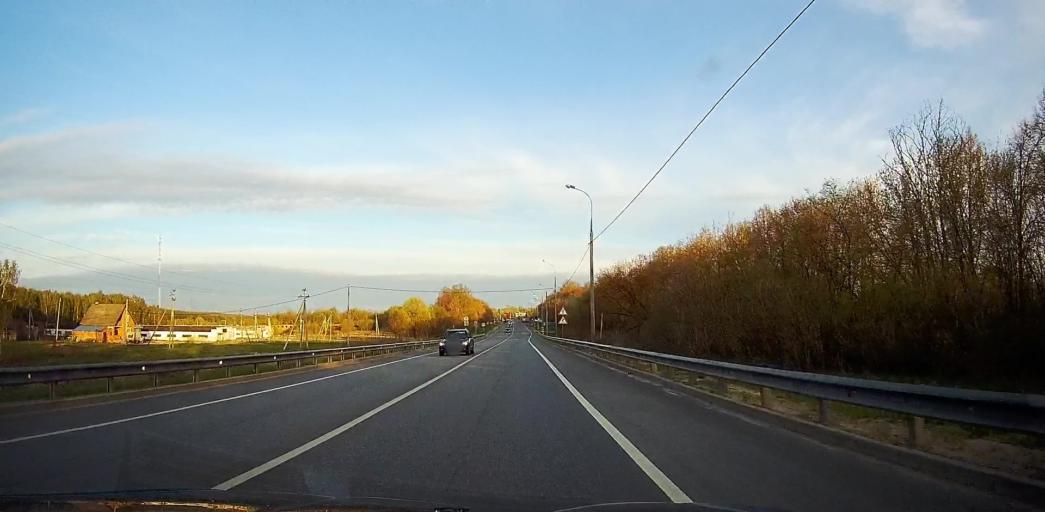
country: RU
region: Moskovskaya
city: Troitskoye
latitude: 55.2314
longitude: 38.5531
